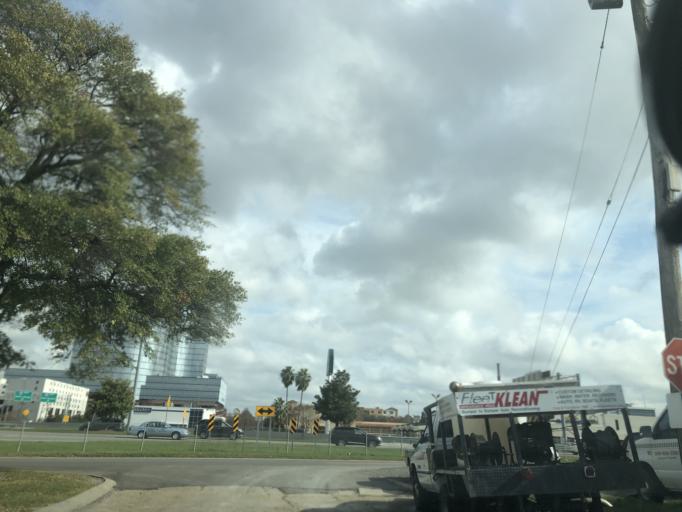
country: US
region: Louisiana
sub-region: Jefferson Parish
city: Metairie
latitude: 29.9949
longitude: -90.1563
